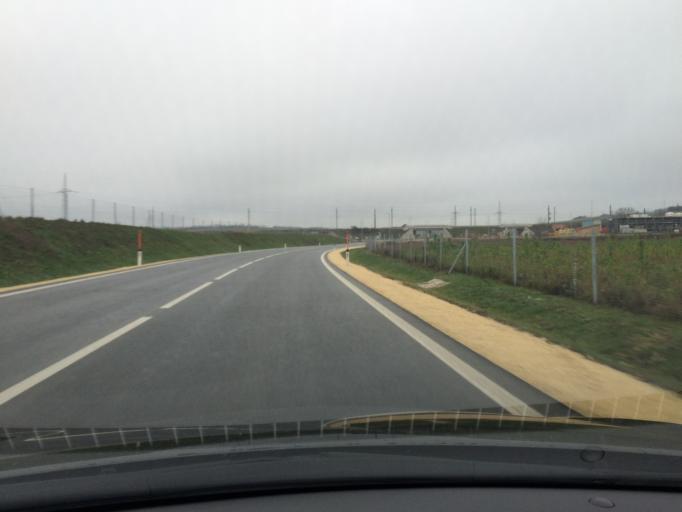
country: AT
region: Lower Austria
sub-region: Politischer Bezirk Mistelbach
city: Mistelbach
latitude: 48.5598
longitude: 16.5557
